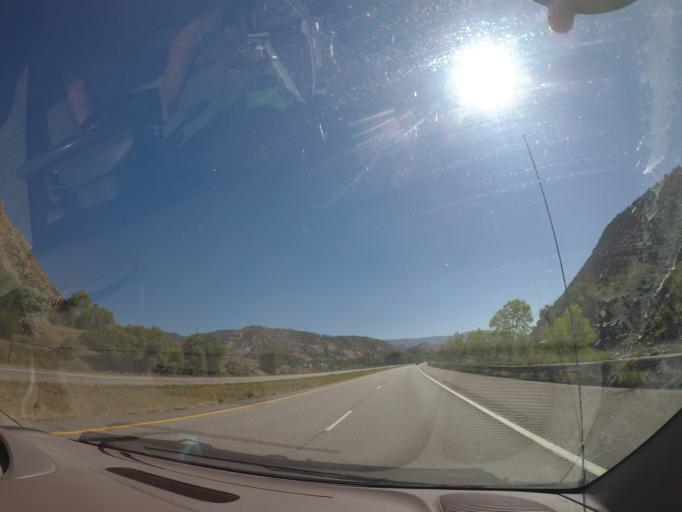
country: US
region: Colorado
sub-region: Garfield County
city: New Castle
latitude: 39.5682
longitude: -107.5450
